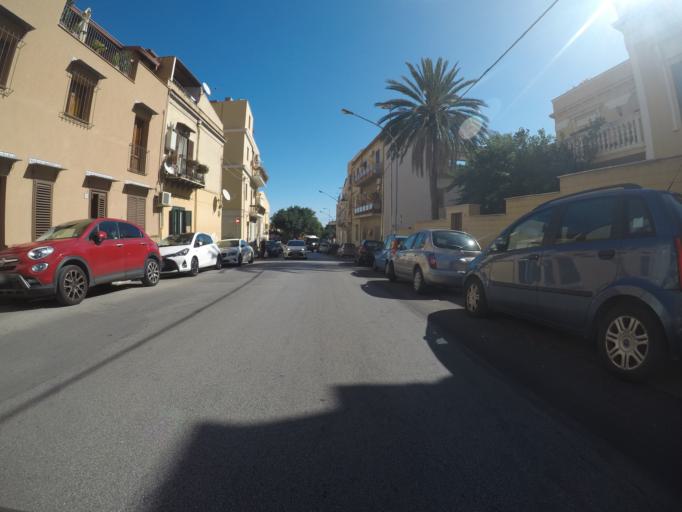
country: IT
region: Sicily
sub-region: Palermo
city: Palermo
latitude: 38.1654
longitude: 13.3666
